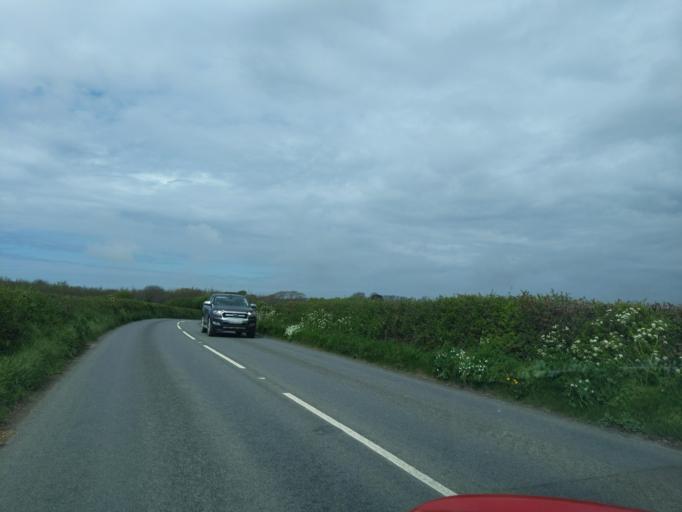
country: GB
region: England
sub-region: Cornwall
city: Wadebridge
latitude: 50.5544
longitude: -4.8643
